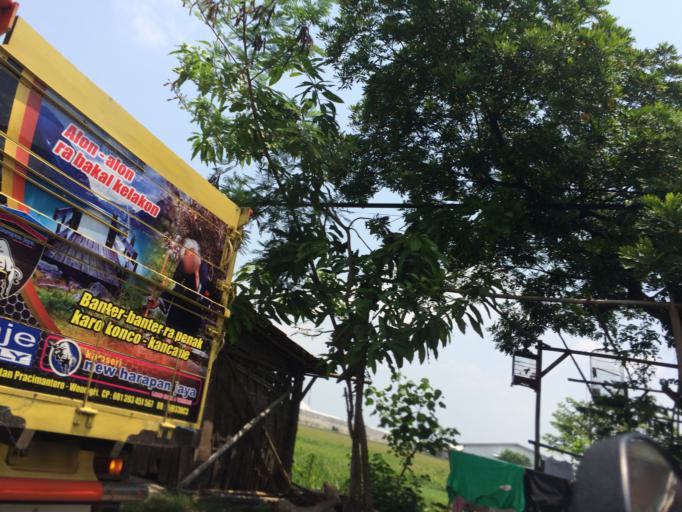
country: ID
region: Central Java
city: Grogol
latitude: -7.6160
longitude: 110.8234
